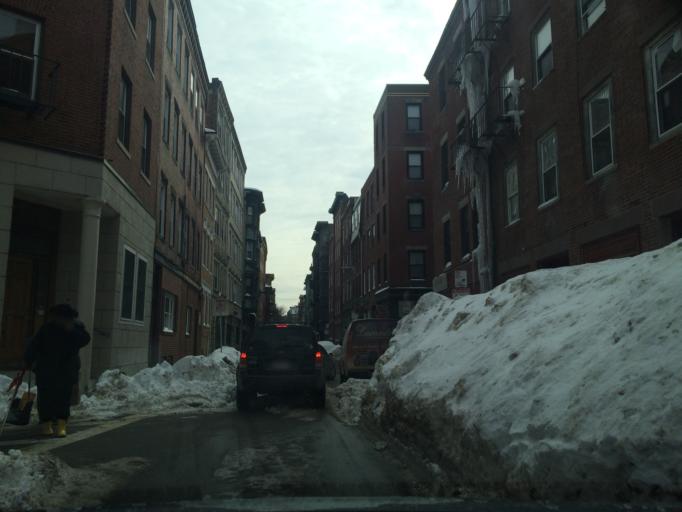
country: US
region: Massachusetts
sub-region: Suffolk County
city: Boston
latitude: 42.3660
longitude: -71.0567
